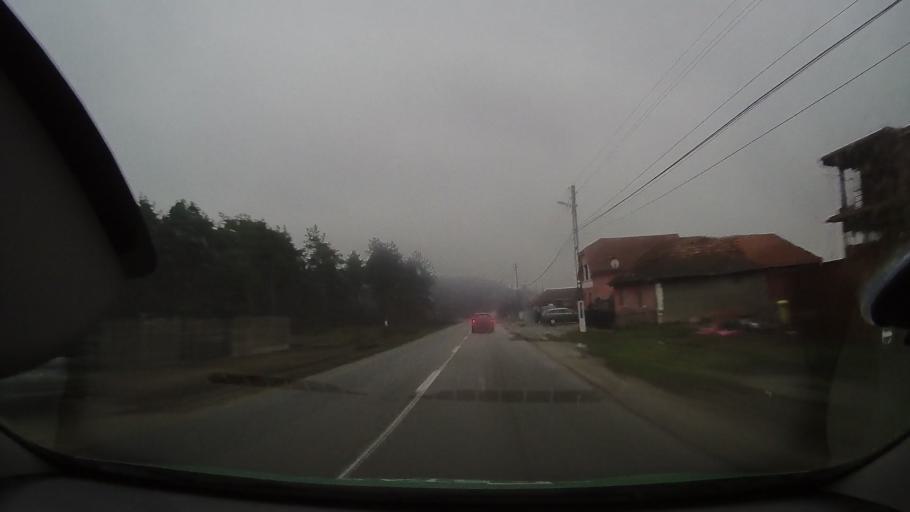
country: RO
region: Arad
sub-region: Comuna Craiova
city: Craiova
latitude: 46.5725
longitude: 21.9731
